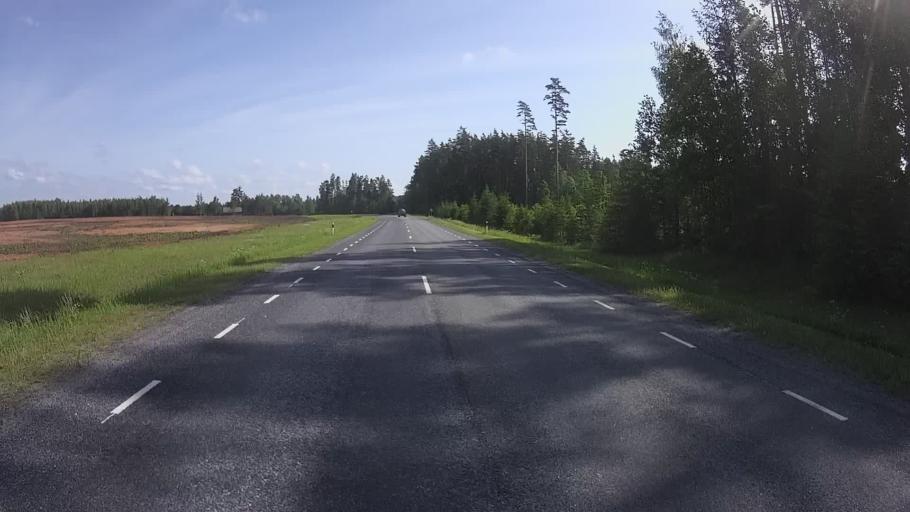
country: EE
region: Valgamaa
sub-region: Torva linn
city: Torva
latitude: 58.0308
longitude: 25.9682
